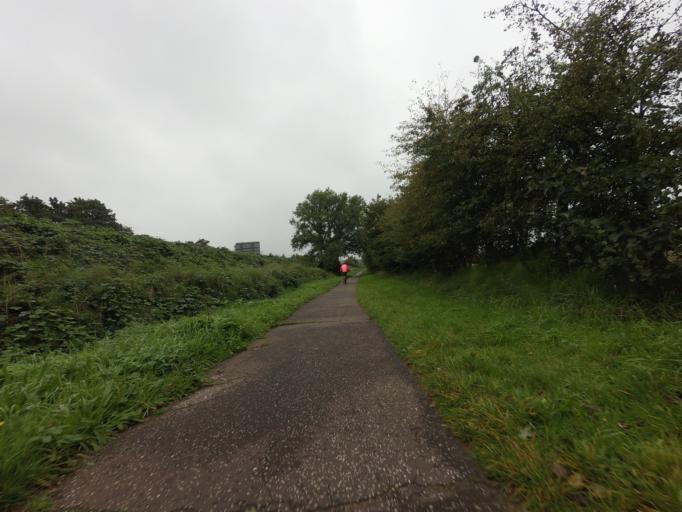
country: GB
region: England
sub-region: Norfolk
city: Dersingham
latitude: 52.8080
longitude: 0.4848
